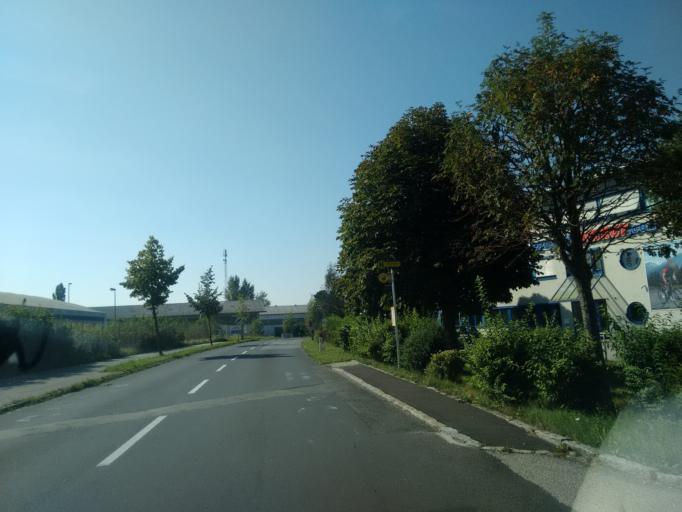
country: AT
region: Upper Austria
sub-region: Wels Stadt
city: Wels
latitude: 48.1794
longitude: 14.0472
